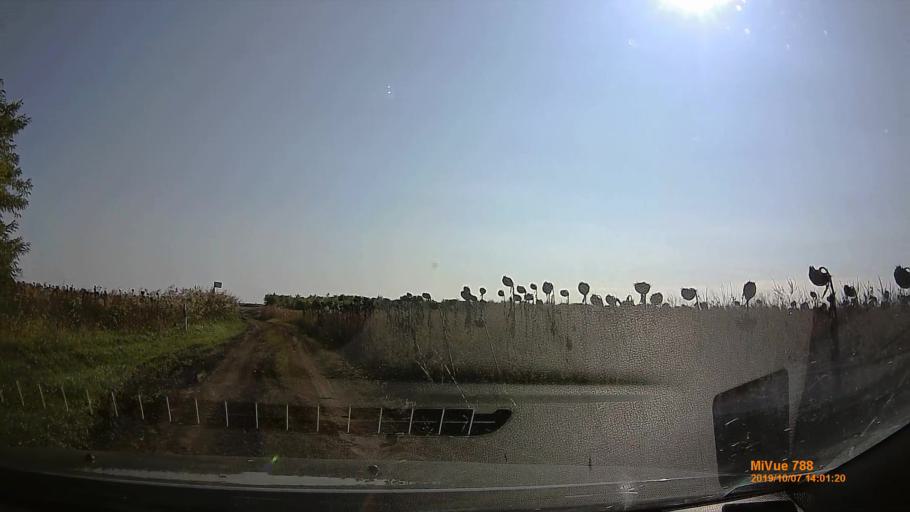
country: HU
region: Jasz-Nagykun-Szolnok
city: Cserkeszolo
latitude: 46.8829
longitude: 20.2173
